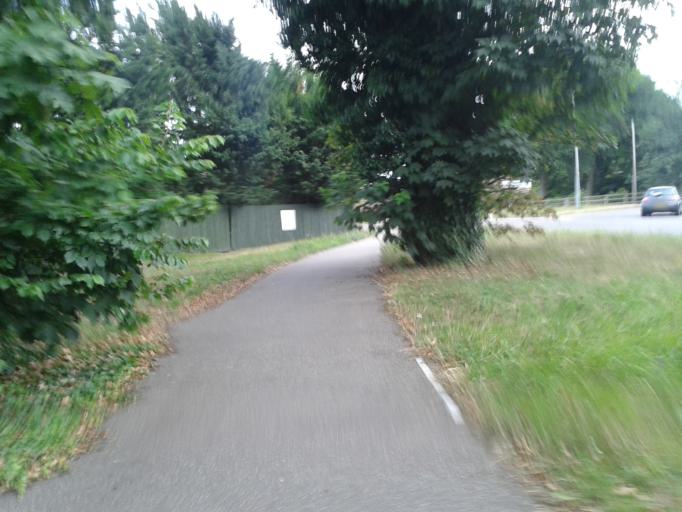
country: GB
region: England
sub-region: Cambridgeshire
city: Sawston
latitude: 52.1660
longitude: 0.1614
